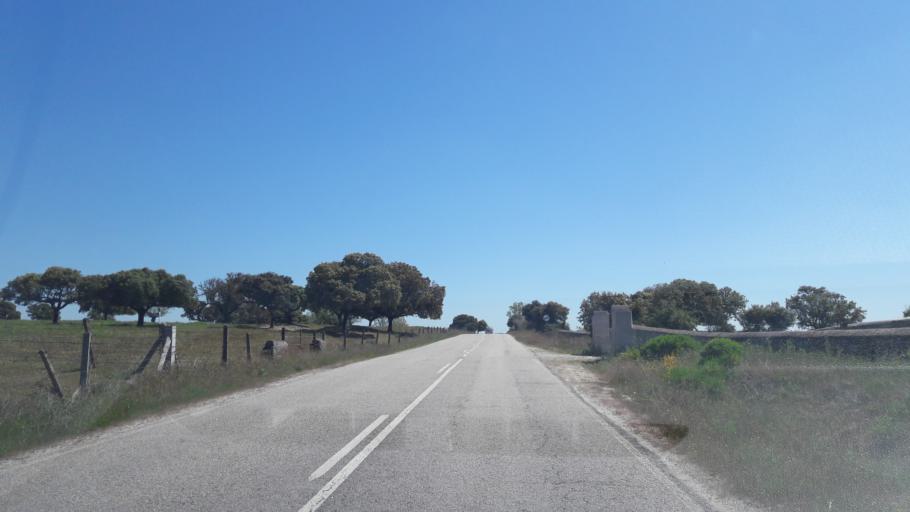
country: ES
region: Castille and Leon
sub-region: Provincia de Salamanca
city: Villarmuerto
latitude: 41.0492
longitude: -6.3806
